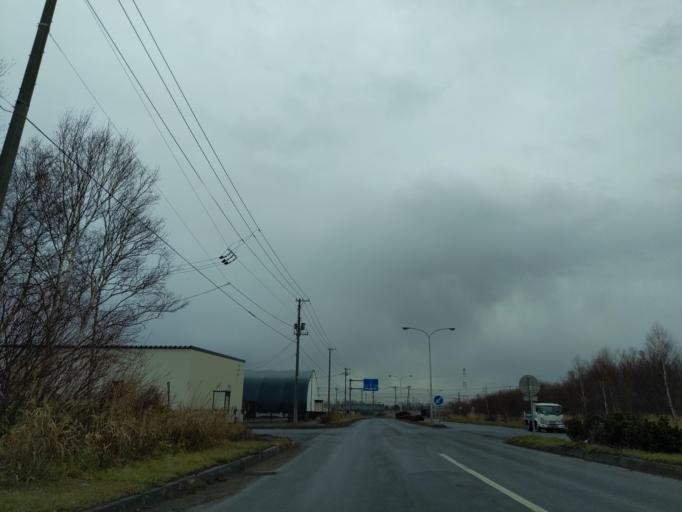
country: JP
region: Hokkaido
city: Ishikari
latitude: 43.1881
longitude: 141.3043
